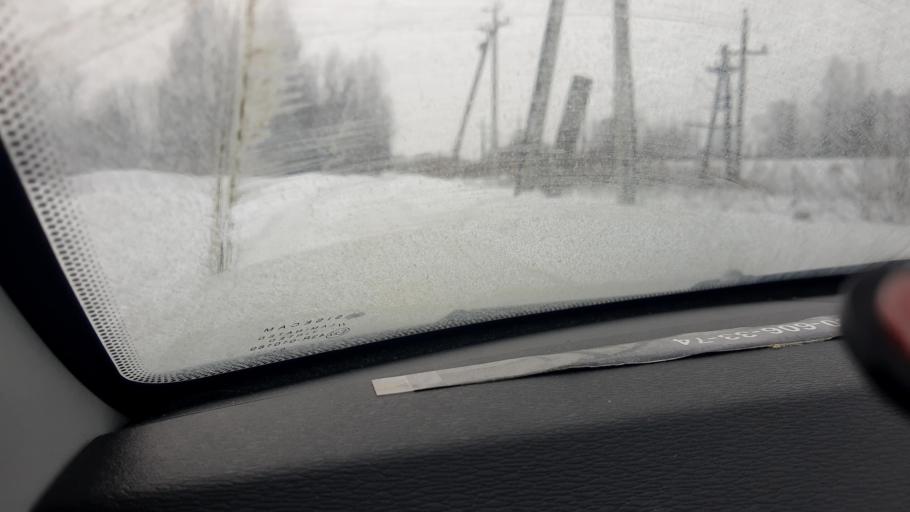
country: RU
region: Nizjnij Novgorod
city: Sitniki
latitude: 56.5246
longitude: 44.0527
